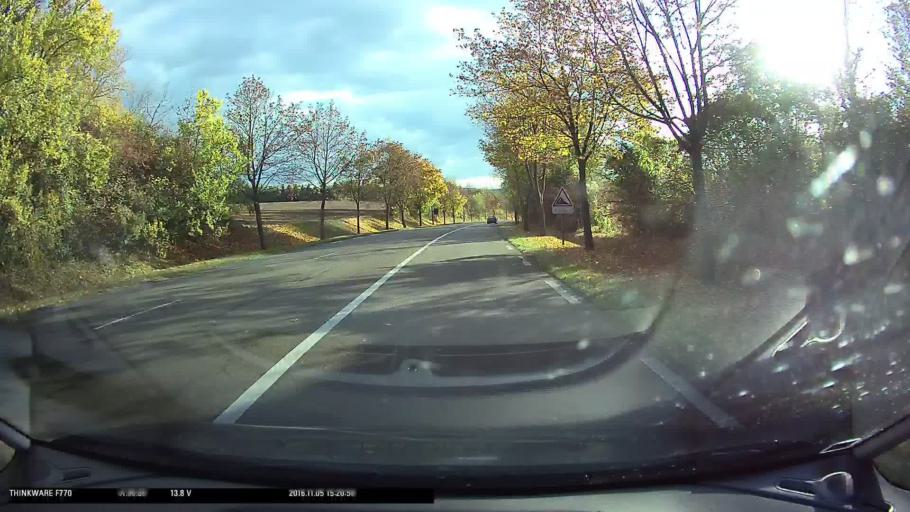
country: FR
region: Ile-de-France
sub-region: Departement du Val-d'Oise
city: Sagy
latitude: 49.0590
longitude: 1.9629
